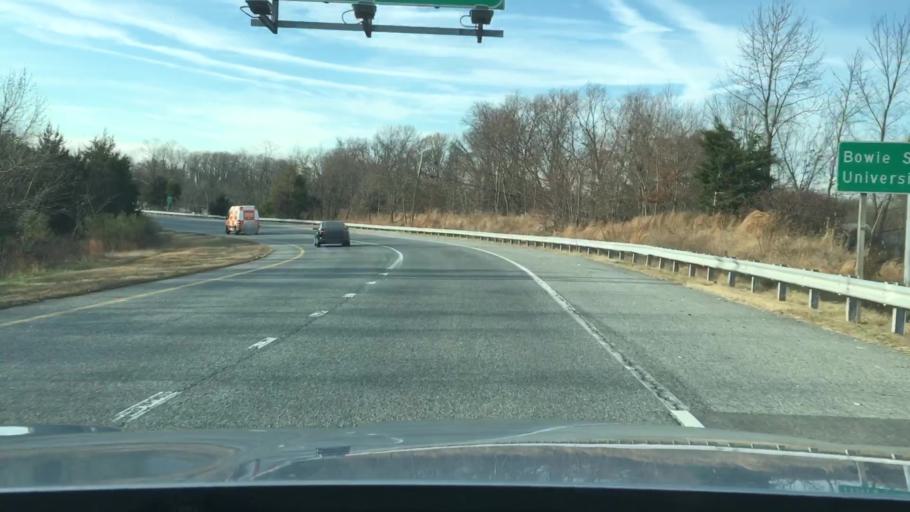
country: US
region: Maryland
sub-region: Prince George's County
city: Bowie
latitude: 38.9548
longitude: -76.7416
